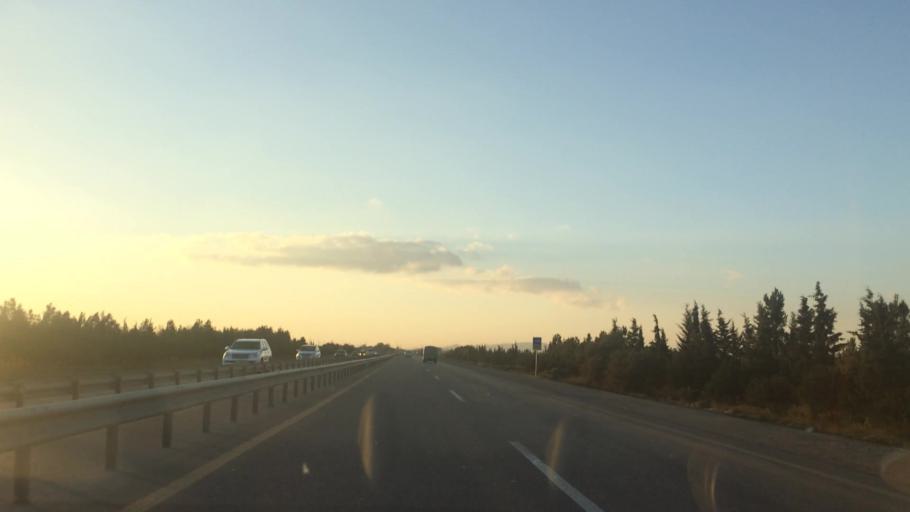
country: AZ
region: Haciqabul
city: Haciqabul
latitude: 40.0234
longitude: 49.1177
